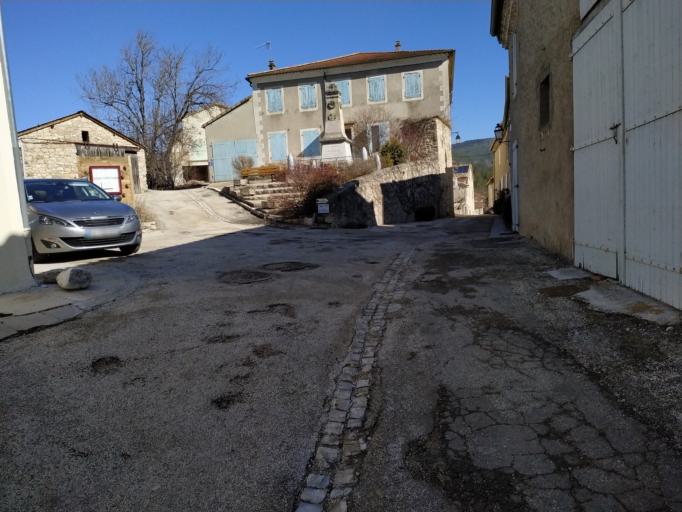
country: FR
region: Provence-Alpes-Cote d'Azur
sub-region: Departement des Hautes-Alpes
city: Serres
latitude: 44.5045
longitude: 5.5725
